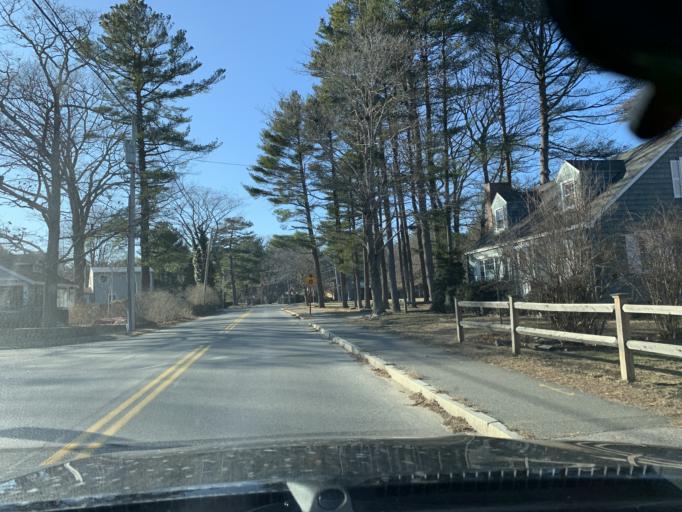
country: US
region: Massachusetts
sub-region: Essex County
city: Essex
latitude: 42.5833
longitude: -70.7793
